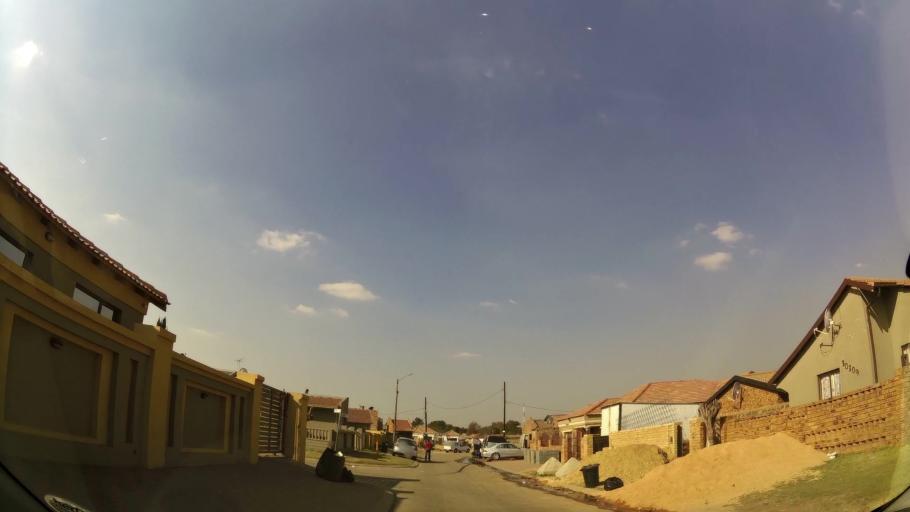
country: ZA
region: Gauteng
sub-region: Ekurhuleni Metropolitan Municipality
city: Brakpan
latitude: -26.1604
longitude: 28.4045
